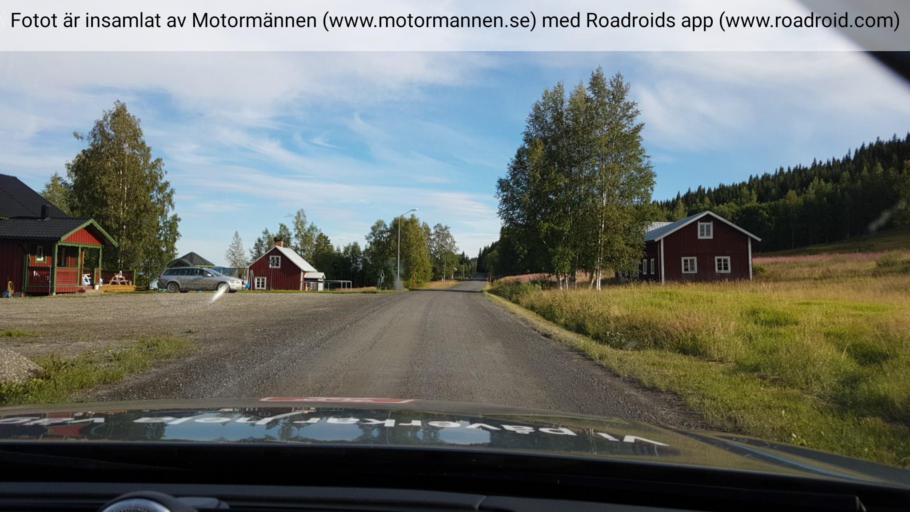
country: SE
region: Jaemtland
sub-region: Stroemsunds Kommun
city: Stroemsund
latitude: 64.1139
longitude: 15.8129
